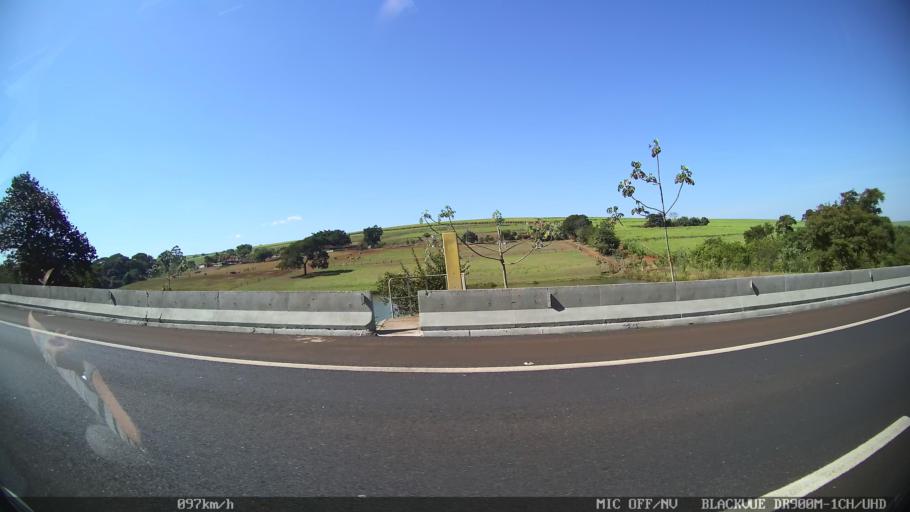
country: BR
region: Sao Paulo
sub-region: Franca
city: Franca
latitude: -20.7024
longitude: -47.5017
